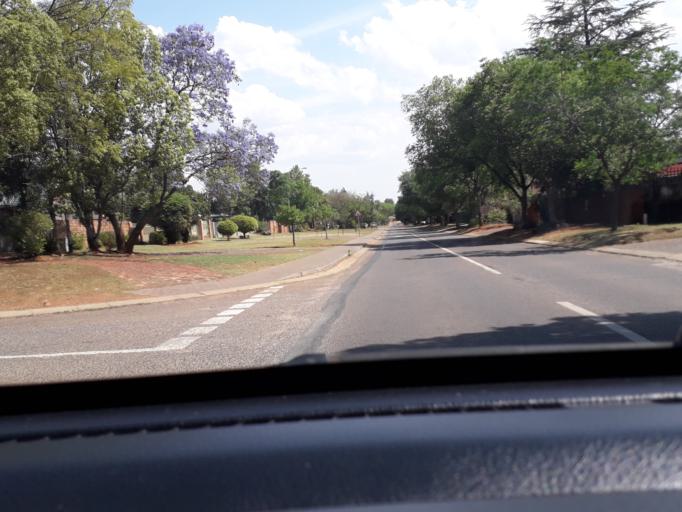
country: ZA
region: Gauteng
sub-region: City of Tshwane Metropolitan Municipality
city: Centurion
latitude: -25.8415
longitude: 28.2382
